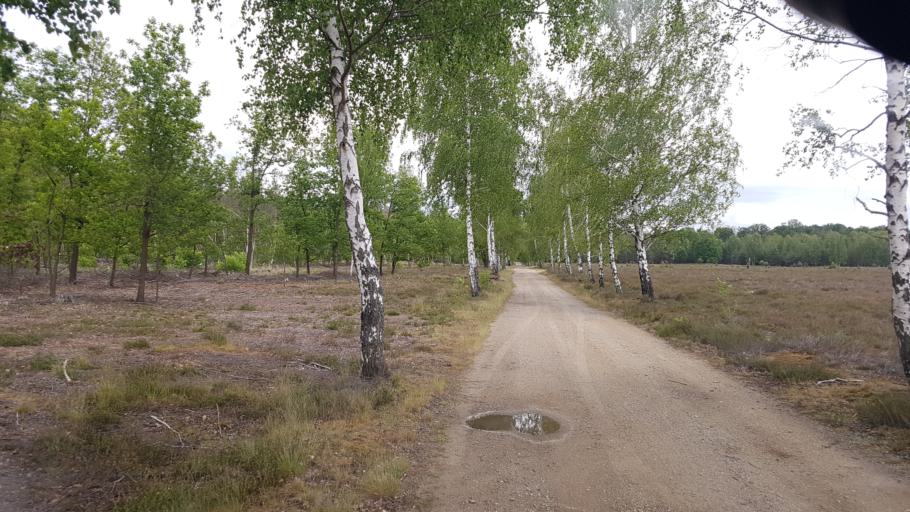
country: DE
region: Brandenburg
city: Hohenleipisch
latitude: 51.5336
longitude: 13.5387
